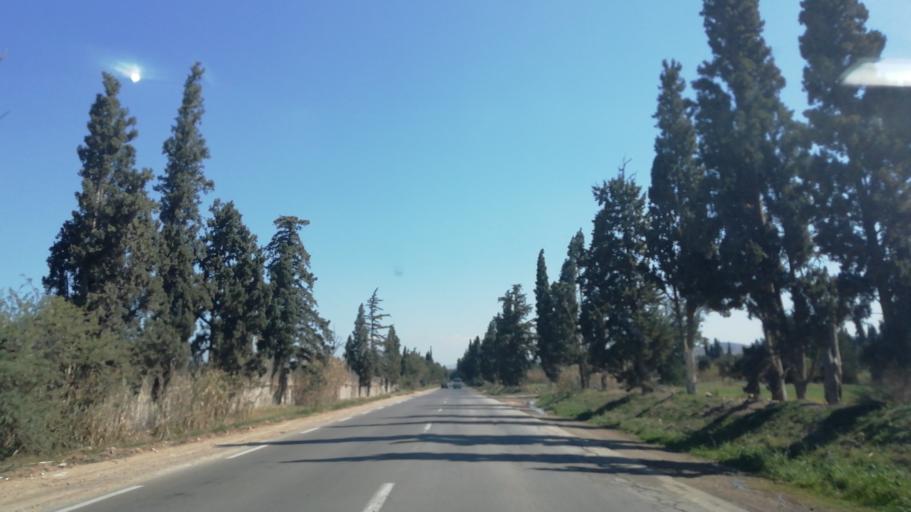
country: DZ
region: Mascara
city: Sig
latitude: 35.5722
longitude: -0.0245
